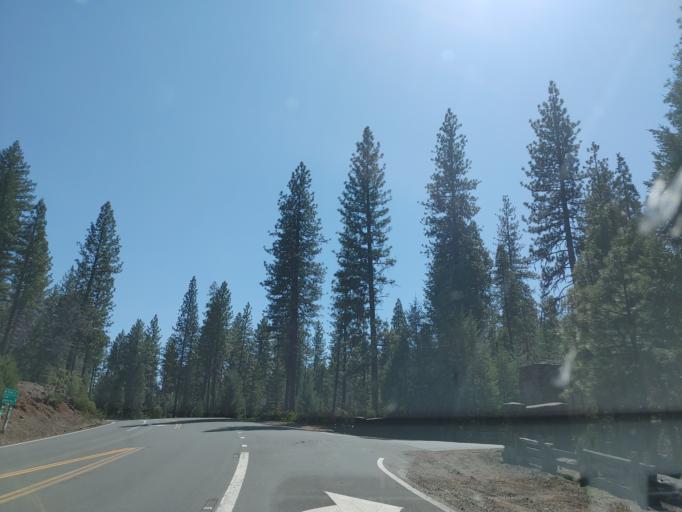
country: US
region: California
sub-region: Shasta County
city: Burney
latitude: 41.0114
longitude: -121.6493
